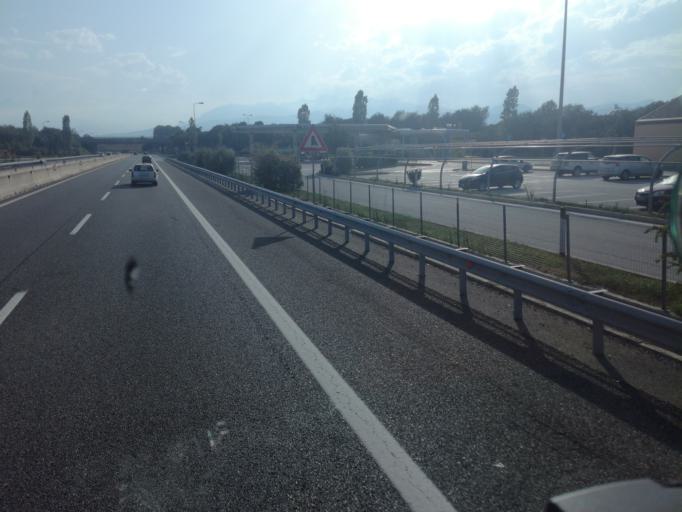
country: IT
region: Piedmont
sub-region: Provincia di Torino
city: Piscina
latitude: 44.9074
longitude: 7.4301
